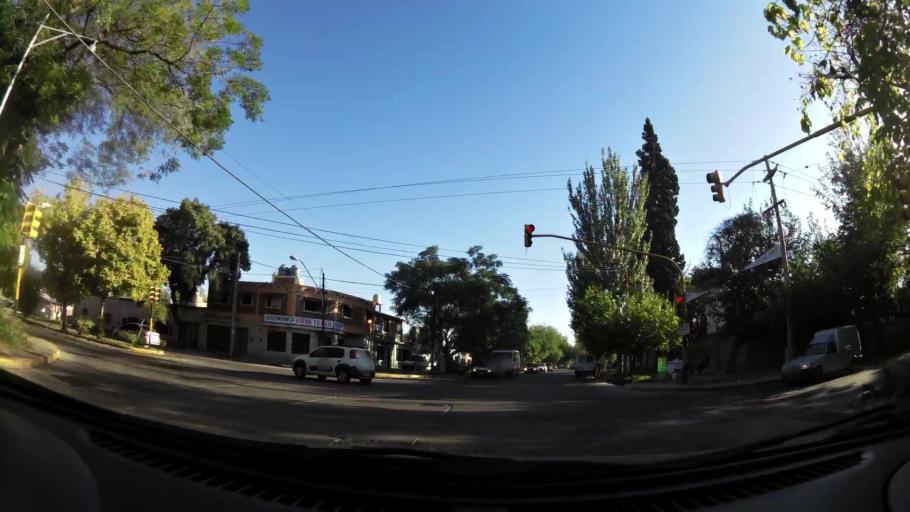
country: AR
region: Mendoza
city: Las Heras
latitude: -32.8674
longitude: -68.8173
